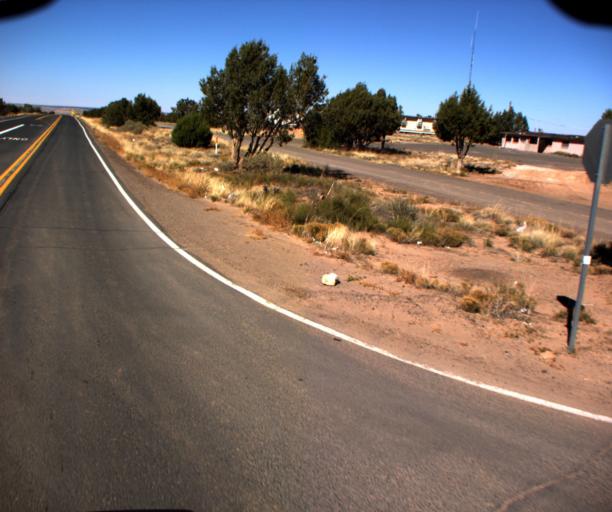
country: US
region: Arizona
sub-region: Navajo County
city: First Mesa
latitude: 35.8445
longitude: -110.5305
